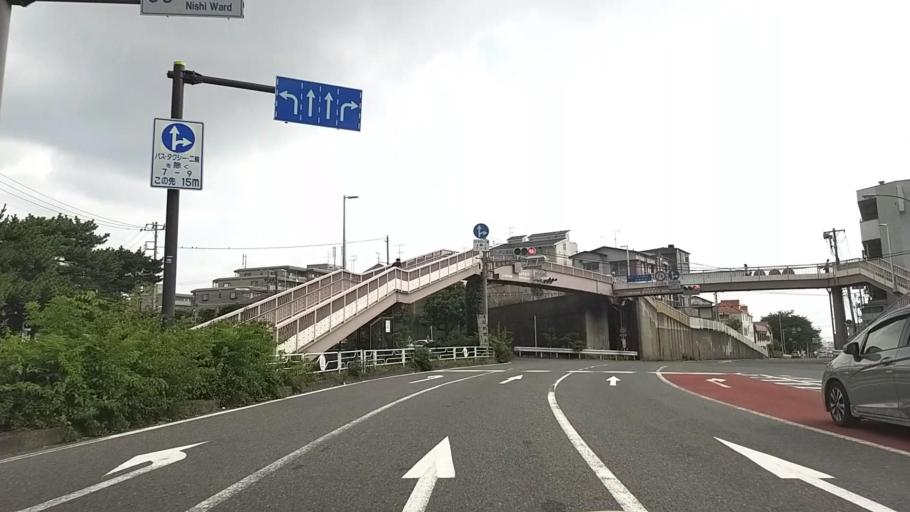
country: JP
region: Kanagawa
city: Yokohama
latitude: 35.4707
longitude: 139.6067
